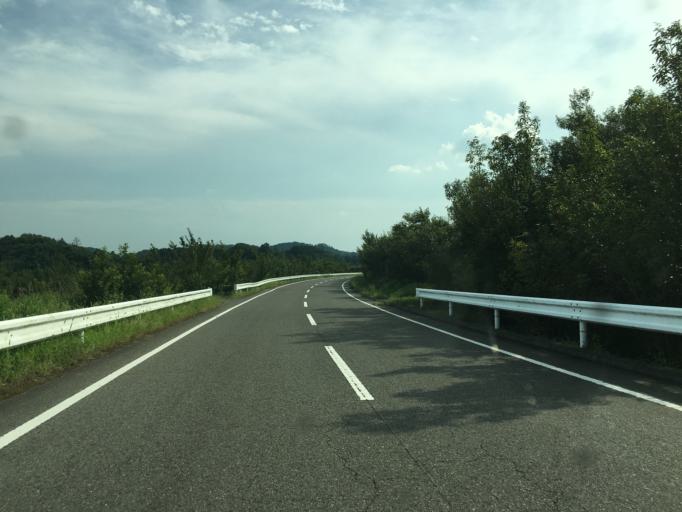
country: JP
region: Fukushima
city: Koriyama
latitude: 37.3820
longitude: 140.4442
